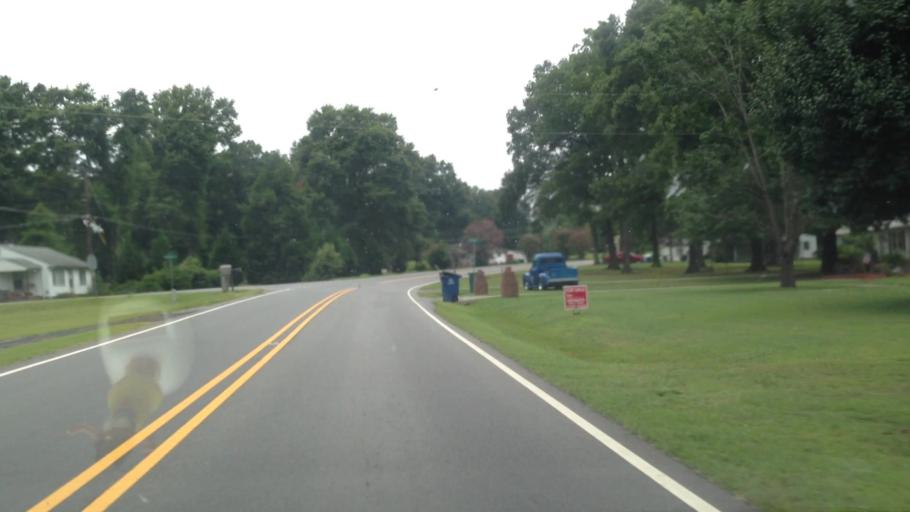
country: US
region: North Carolina
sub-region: Rockingham County
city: Mayodan
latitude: 36.4131
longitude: -80.0121
